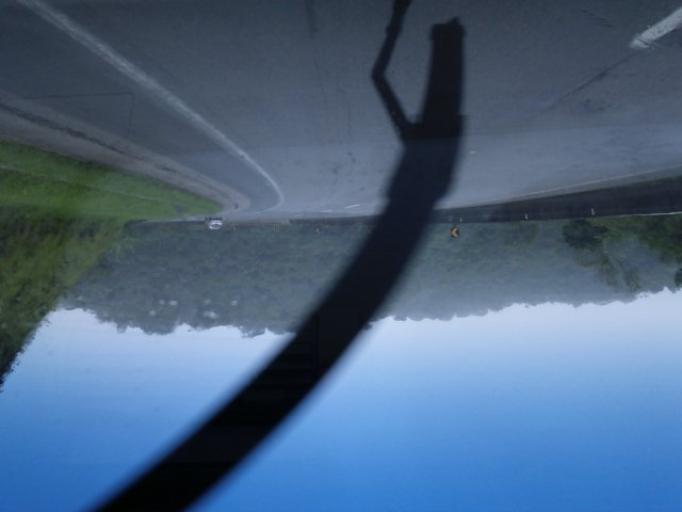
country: BR
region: Parana
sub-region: Antonina
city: Antonina
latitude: -25.1077
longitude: -48.7879
